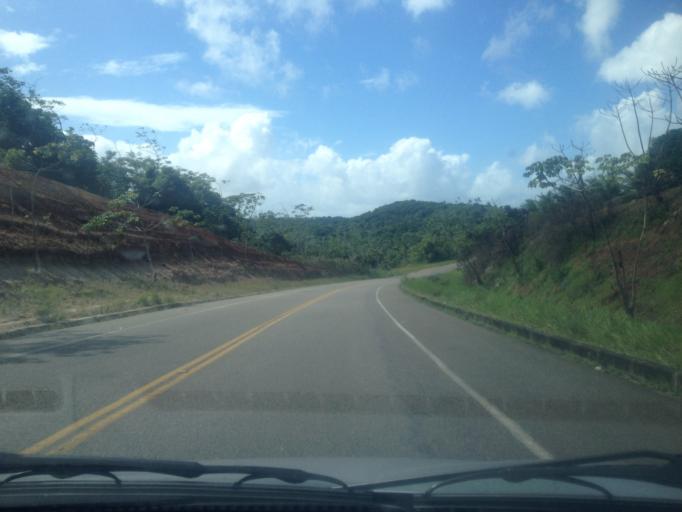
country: BR
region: Bahia
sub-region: Conde
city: Conde
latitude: -11.7761
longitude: -37.6102
